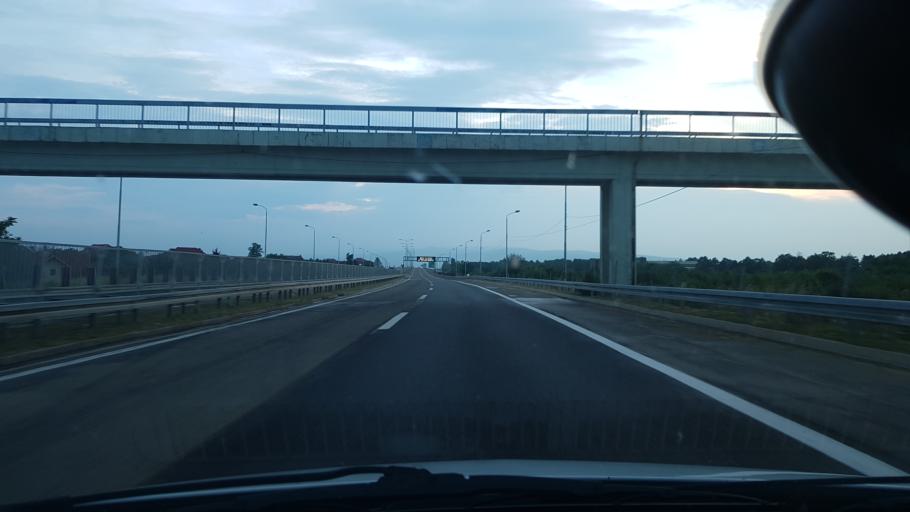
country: RS
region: Central Serbia
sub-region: Nisavski Okrug
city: Nis
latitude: 43.3467
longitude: 21.8741
